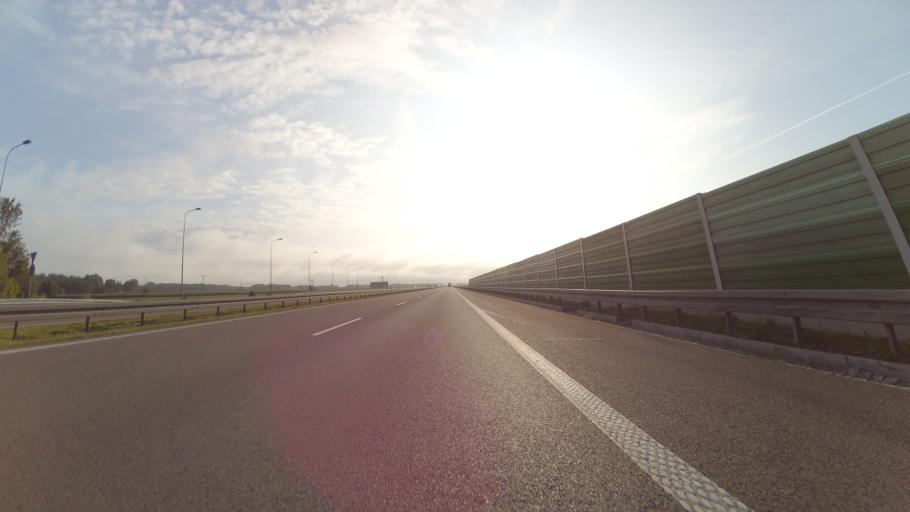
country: PL
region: Podlasie
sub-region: Powiat bialostocki
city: Choroszcz
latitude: 53.1583
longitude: 22.8867
